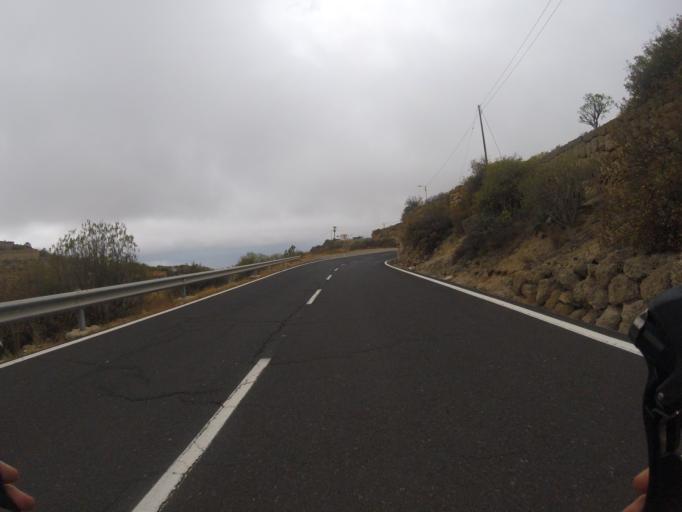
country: ES
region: Canary Islands
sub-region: Provincia de Santa Cruz de Tenerife
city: Fasnia
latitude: 28.2148
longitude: -16.4523
